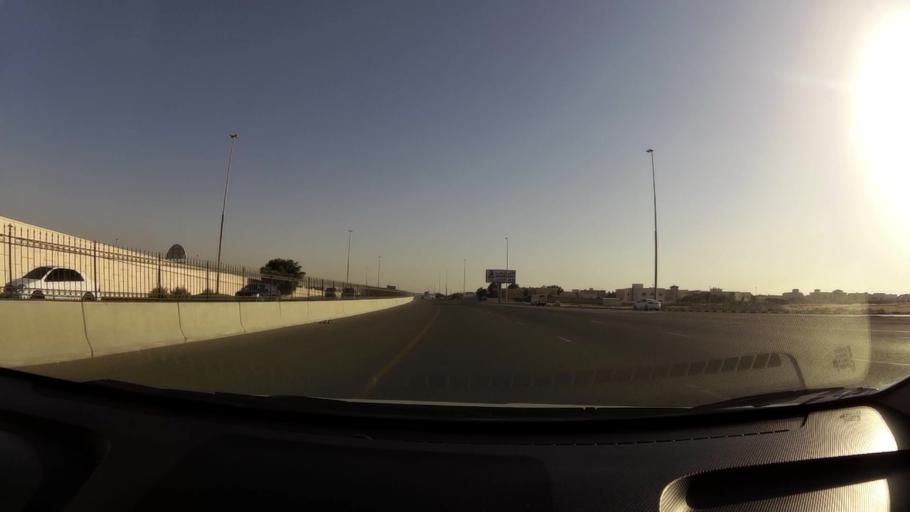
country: AE
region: Ash Shariqah
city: Sharjah
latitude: 25.3558
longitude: 55.4805
